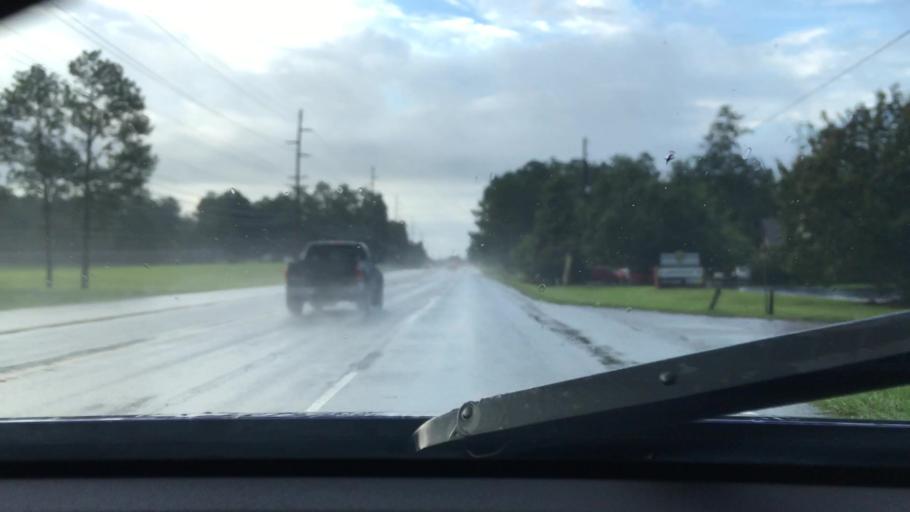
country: US
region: South Carolina
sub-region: Lexington County
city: Saint Andrews
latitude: 34.0748
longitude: -81.1307
